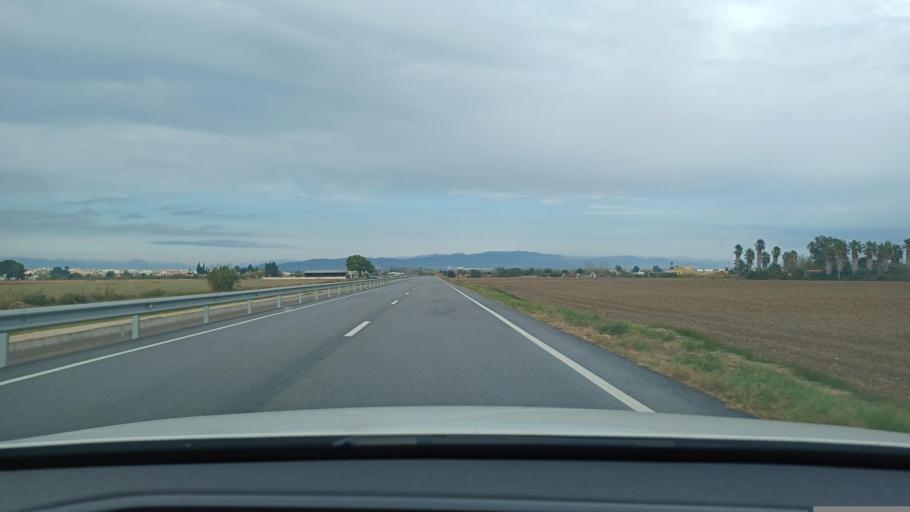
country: ES
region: Catalonia
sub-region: Provincia de Tarragona
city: Amposta
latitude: 40.6877
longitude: 0.5904
